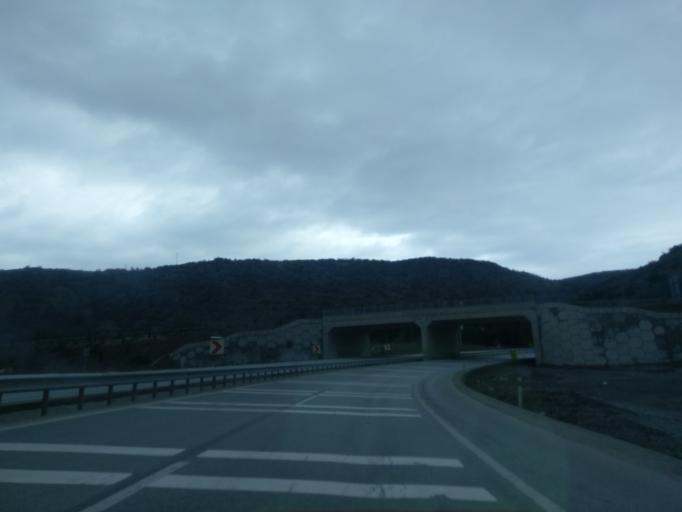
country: TR
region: Kuetahya
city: Sabuncu
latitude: 39.5756
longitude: 30.0847
